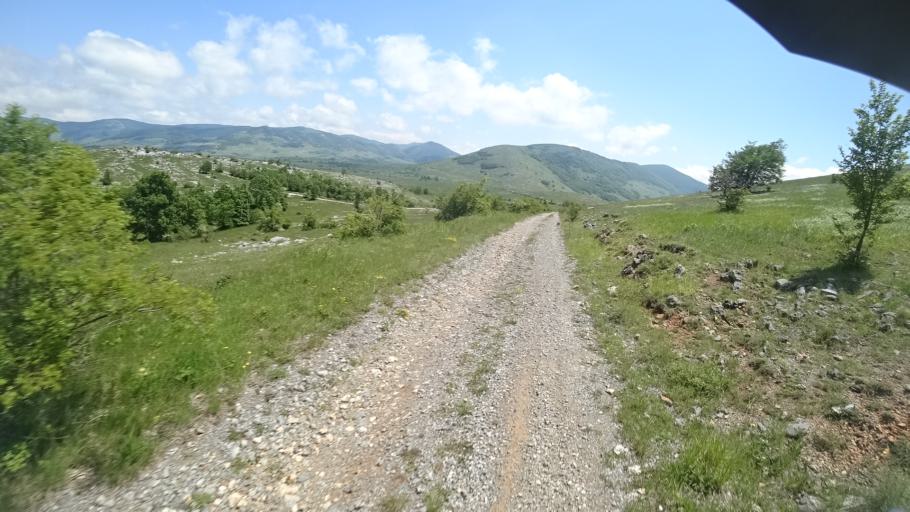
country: HR
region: Zadarska
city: Gracac
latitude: 44.4421
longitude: 15.9164
